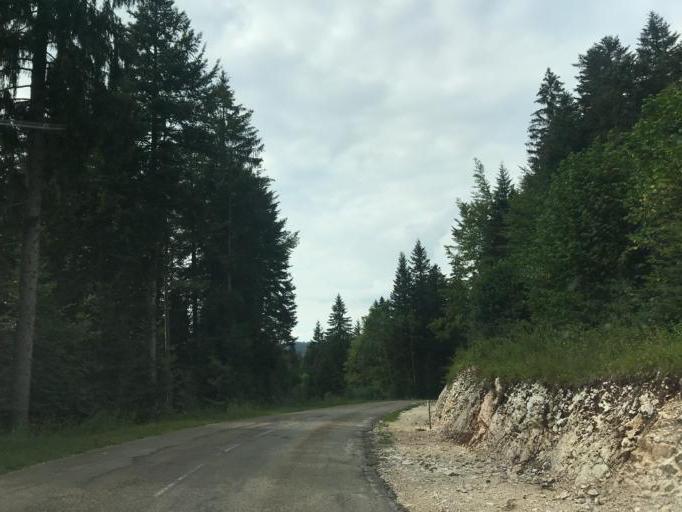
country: FR
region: Franche-Comte
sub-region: Departement du Jura
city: Longchaumois
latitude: 46.5070
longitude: 5.8861
